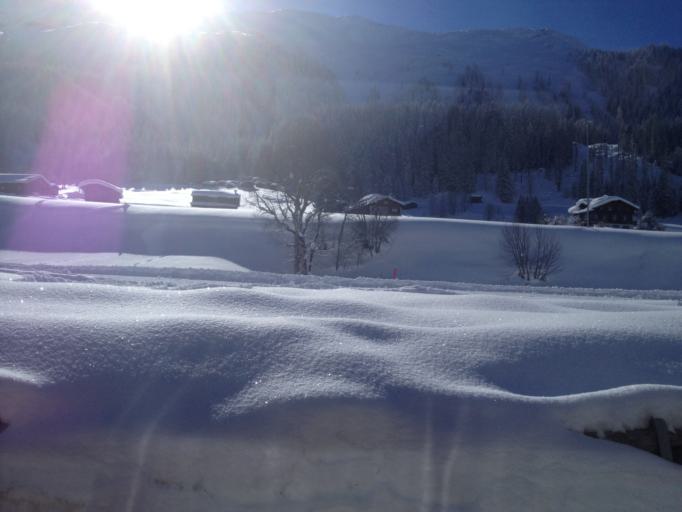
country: CH
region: Grisons
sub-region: Praettigau/Davos District
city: Klosters Serneus
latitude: 46.8626
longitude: 9.9062
